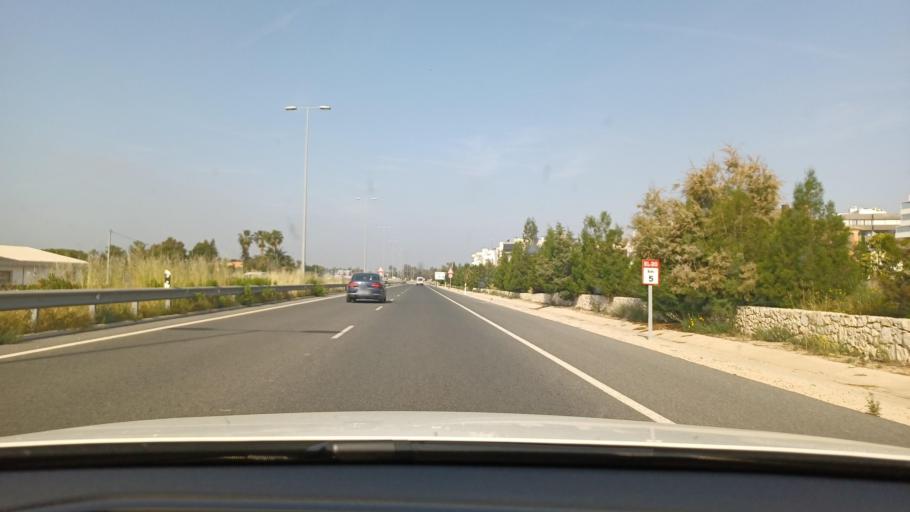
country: ES
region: Valencia
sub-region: Provincia de Alicante
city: Elche
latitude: 38.2608
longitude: -0.6675
